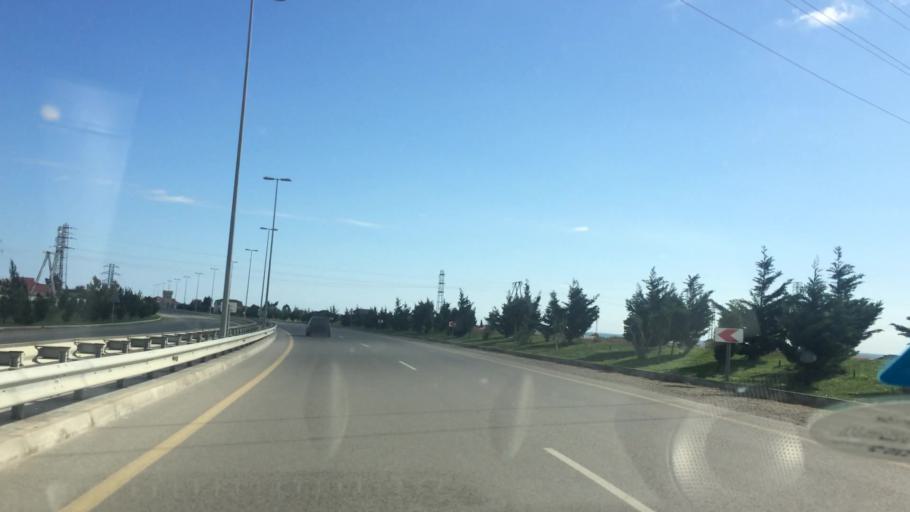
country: AZ
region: Baki
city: Zyrya
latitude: 40.3981
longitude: 50.3271
